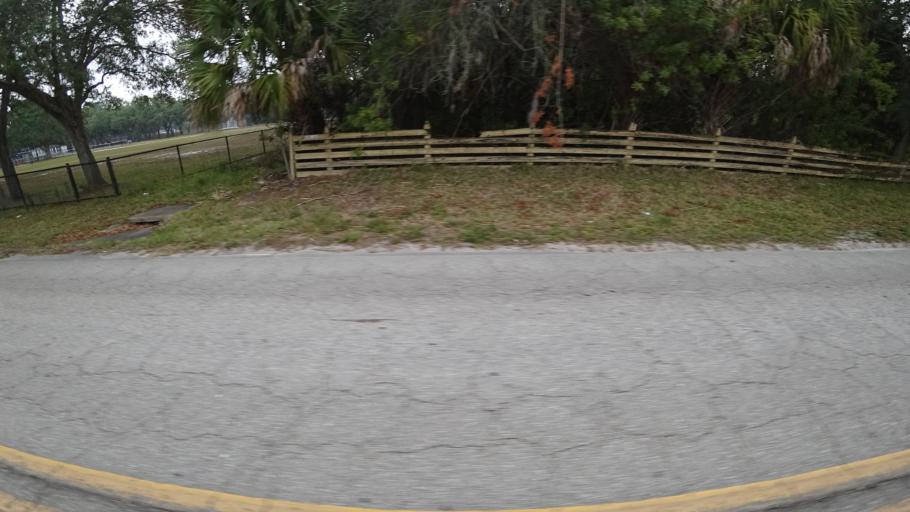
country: US
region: Florida
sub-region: Manatee County
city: Samoset
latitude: 27.4492
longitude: -82.5161
